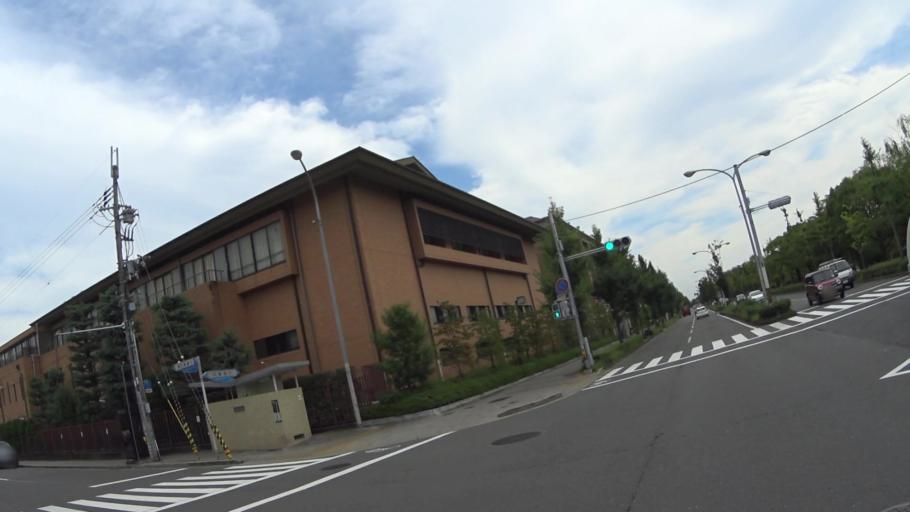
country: JP
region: Kyoto
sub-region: Kyoto-shi
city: Kamigyo-ku
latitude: 35.0257
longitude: 135.7723
